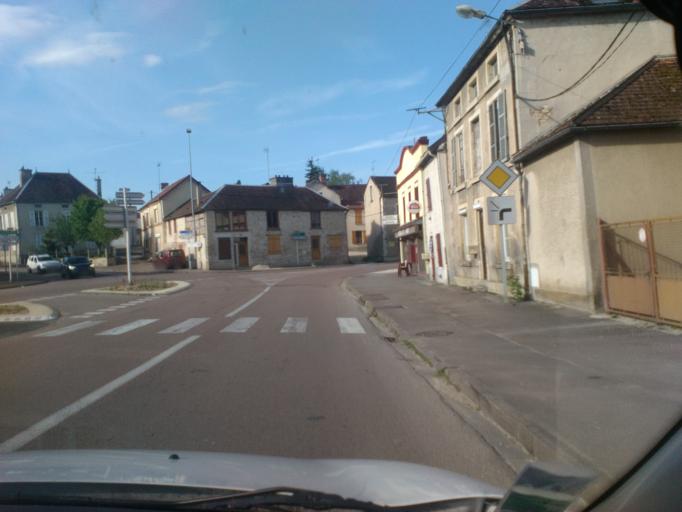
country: FR
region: Champagne-Ardenne
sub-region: Departement de l'Aube
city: Vendeuvre-sur-Barse
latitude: 48.2366
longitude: 4.4642
